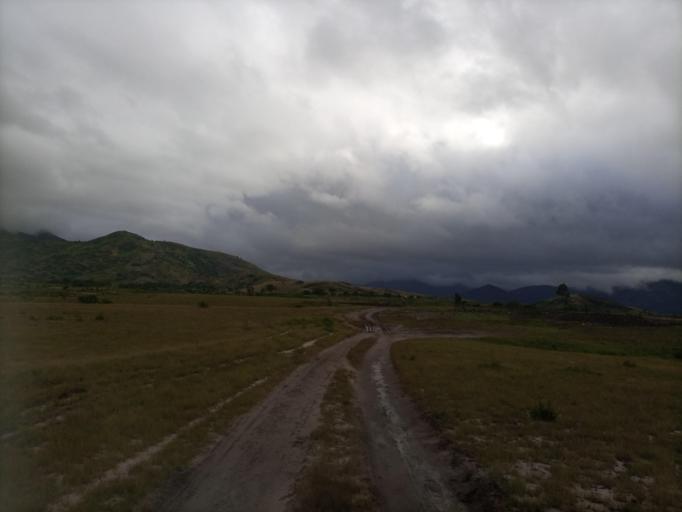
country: MG
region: Anosy
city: Fort Dauphin
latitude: -24.7602
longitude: 47.0737
